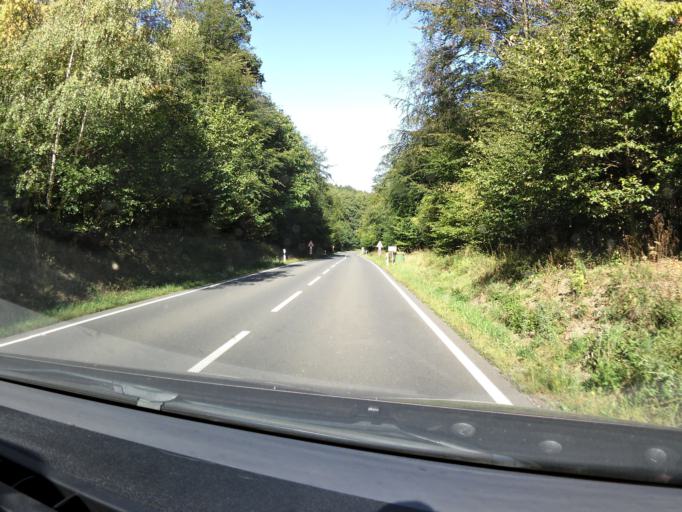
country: DE
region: Saxony-Anhalt
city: Gernrode
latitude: 51.6955
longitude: 11.1328
